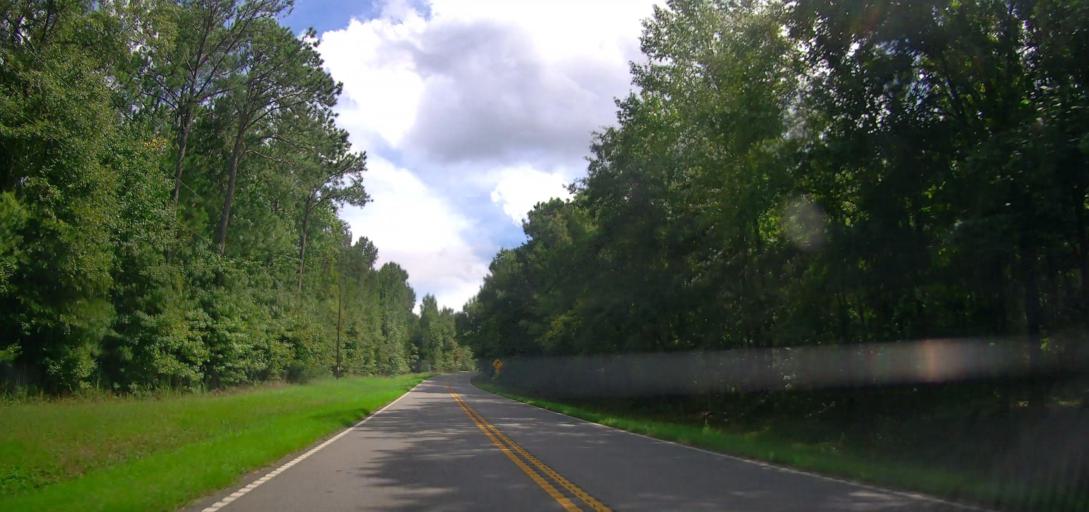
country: US
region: Georgia
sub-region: Talbot County
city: Talbotton
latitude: 32.6278
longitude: -84.4878
